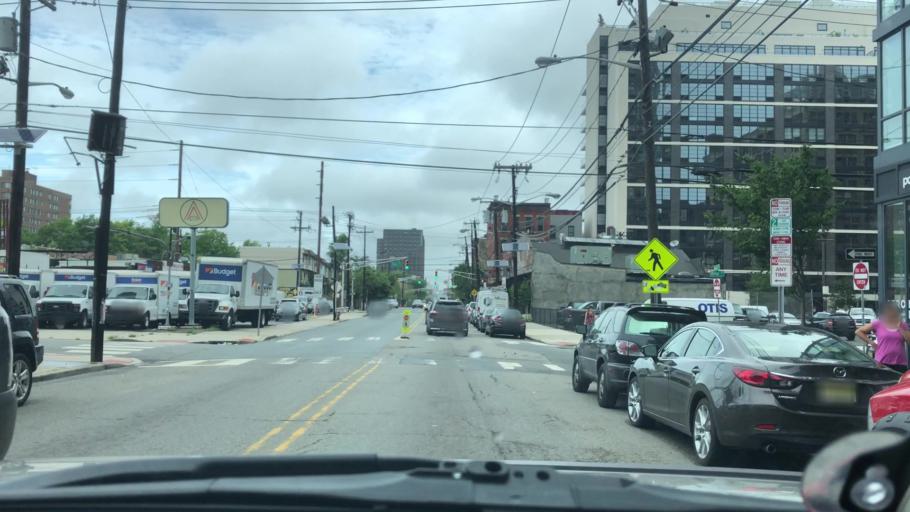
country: US
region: New Jersey
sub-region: Hudson County
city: Hoboken
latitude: 40.7206
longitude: -74.0412
